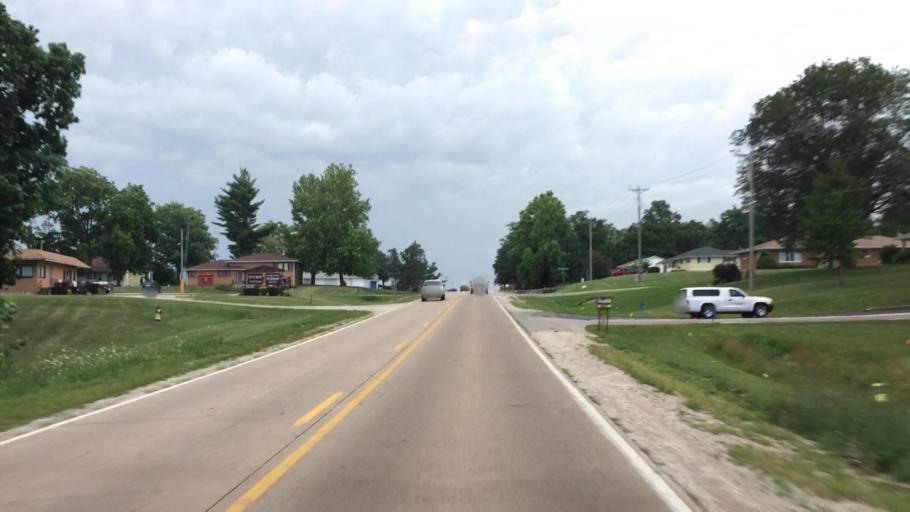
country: US
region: Iowa
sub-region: Lee County
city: Fort Madison
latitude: 40.6467
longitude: -91.3175
